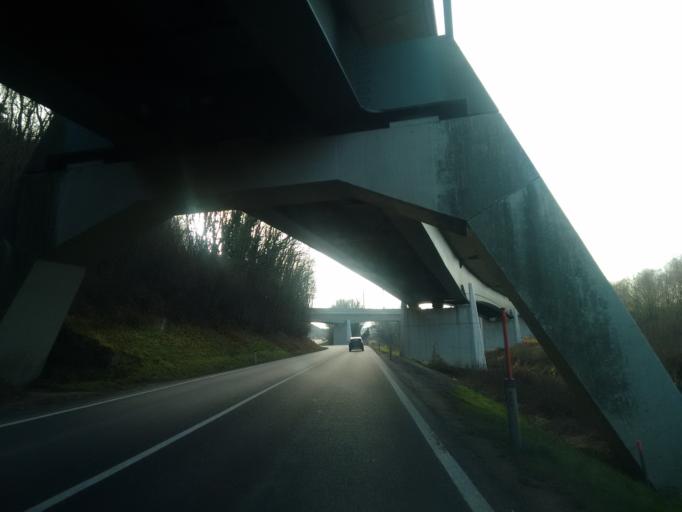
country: AT
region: Lower Austria
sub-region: Politischer Bezirk Melk
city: Melk
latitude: 48.2205
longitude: 15.3172
